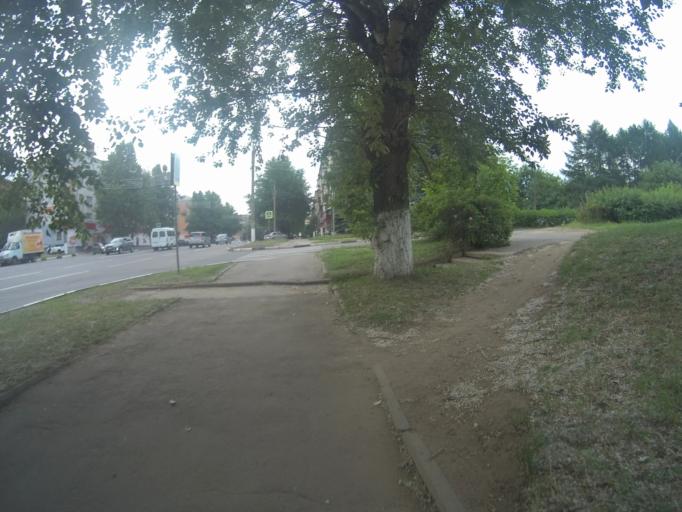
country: RU
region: Vladimir
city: Vladimir
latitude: 56.1393
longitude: 40.3903
